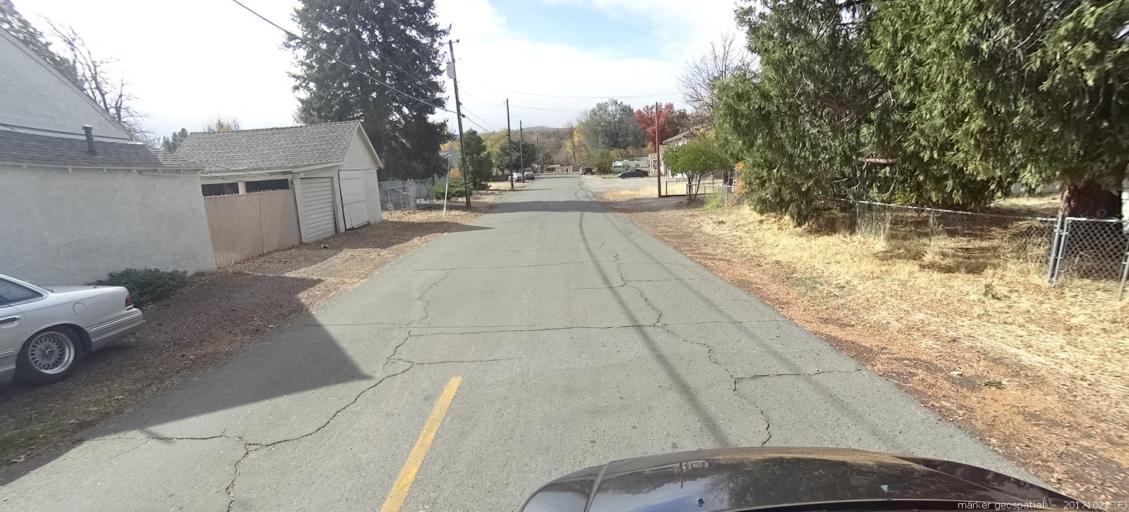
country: US
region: California
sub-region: Shasta County
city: Burney
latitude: 40.8831
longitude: -121.6644
